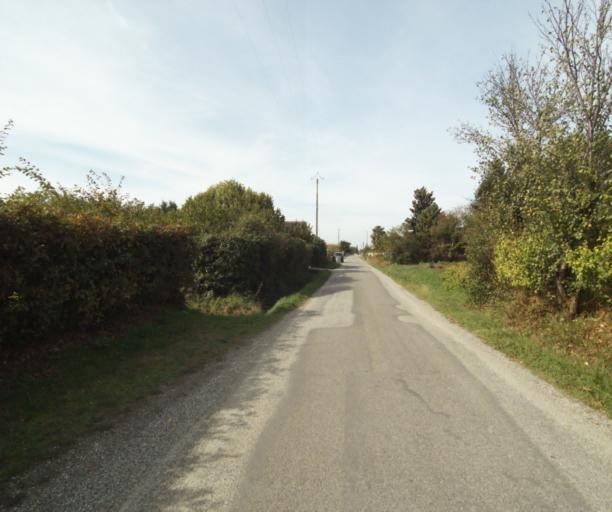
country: FR
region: Midi-Pyrenees
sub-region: Departement du Tarn-et-Garonne
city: Orgueil
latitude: 43.9071
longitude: 1.4079
